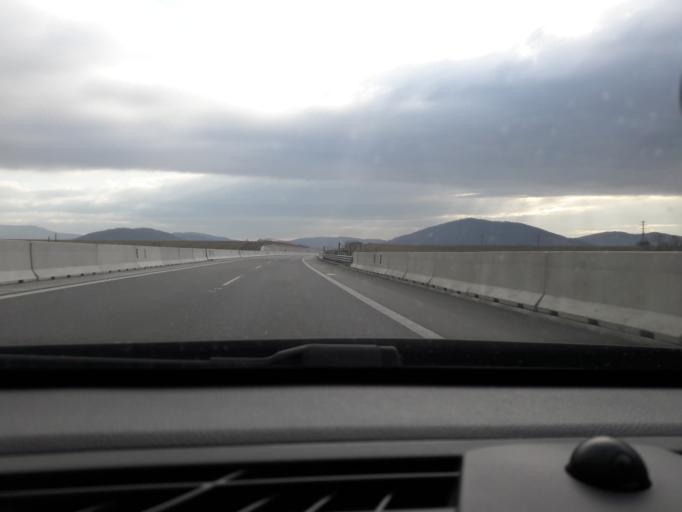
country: SK
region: Banskobystricky
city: Hrochot,Slovakia
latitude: 48.5701
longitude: 19.2950
